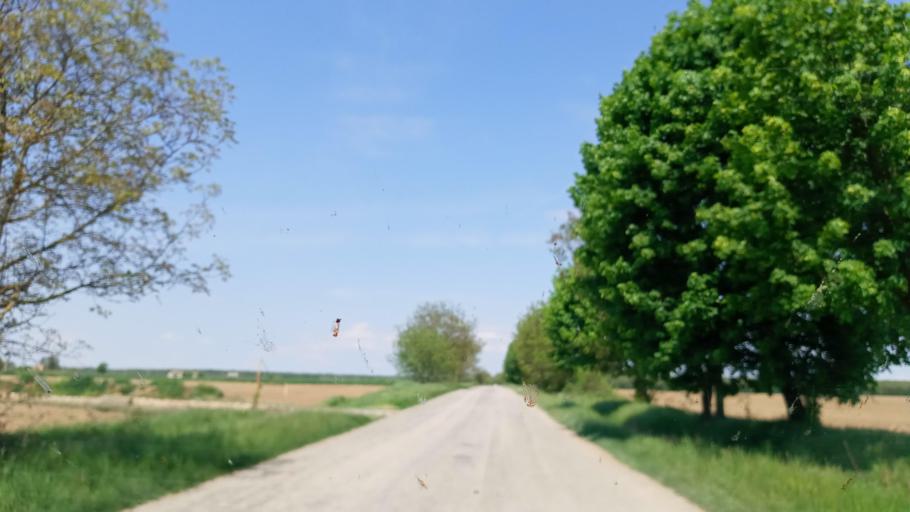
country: HR
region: Osjecko-Baranjska
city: Beli Manastir
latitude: 45.8759
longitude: 18.5793
